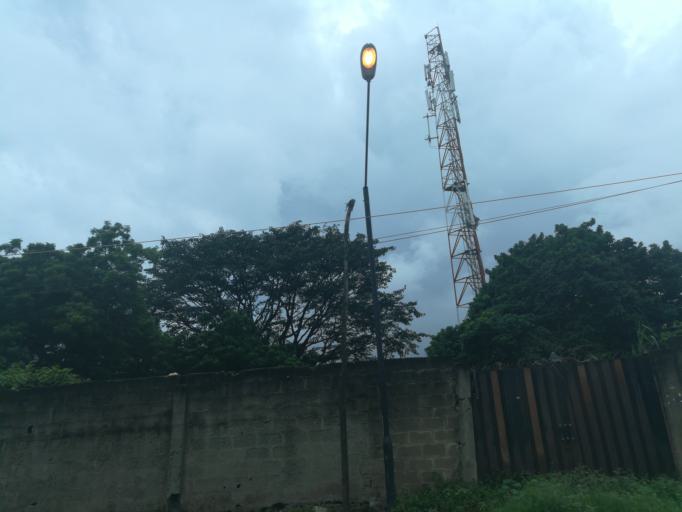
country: NG
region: Lagos
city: Ikeja
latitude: 6.6148
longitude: 3.3436
